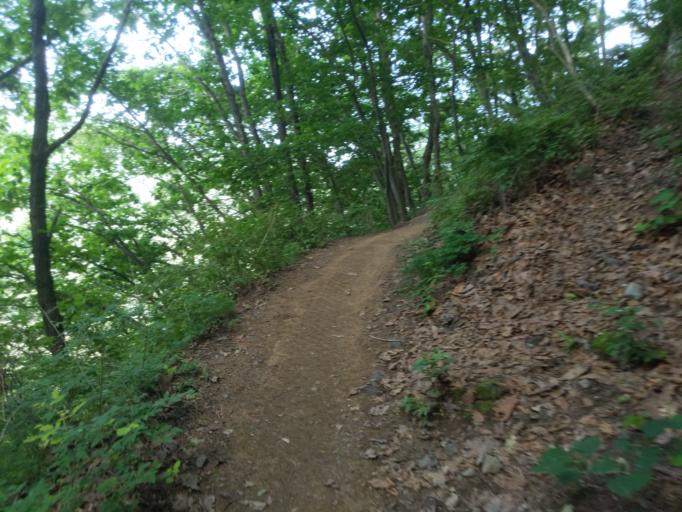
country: KR
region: Daegu
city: Hwawon
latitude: 35.7861
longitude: 128.5464
